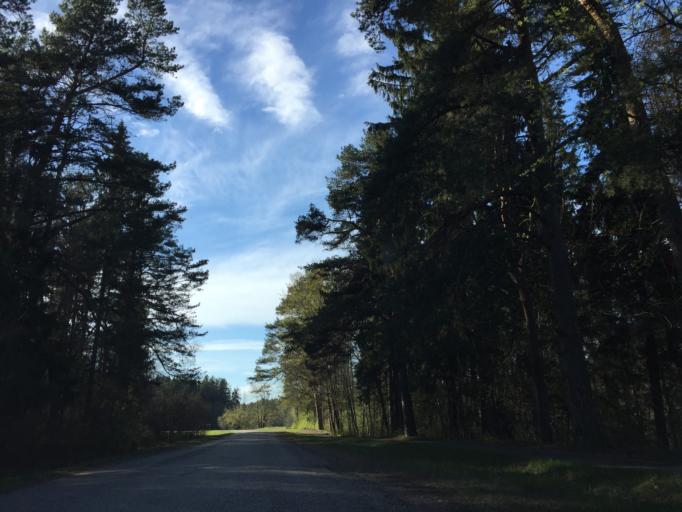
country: LV
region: Valkas Rajons
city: Valka
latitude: 57.7918
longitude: 25.9805
